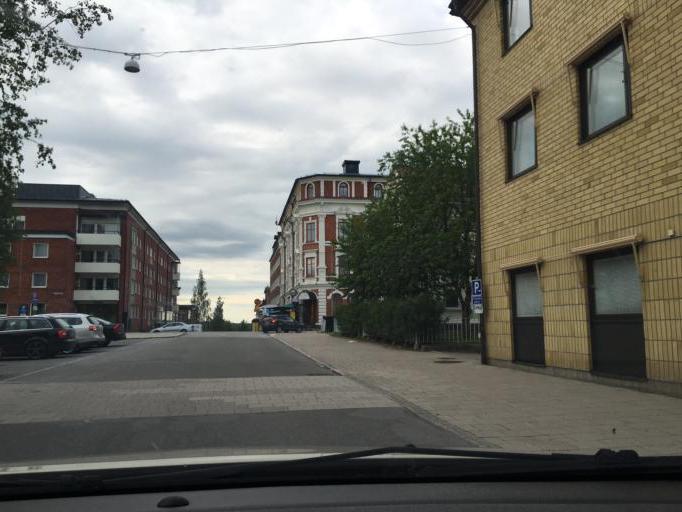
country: SE
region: Norrbotten
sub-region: Lulea Kommun
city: Lulea
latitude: 65.5828
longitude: 22.1504
